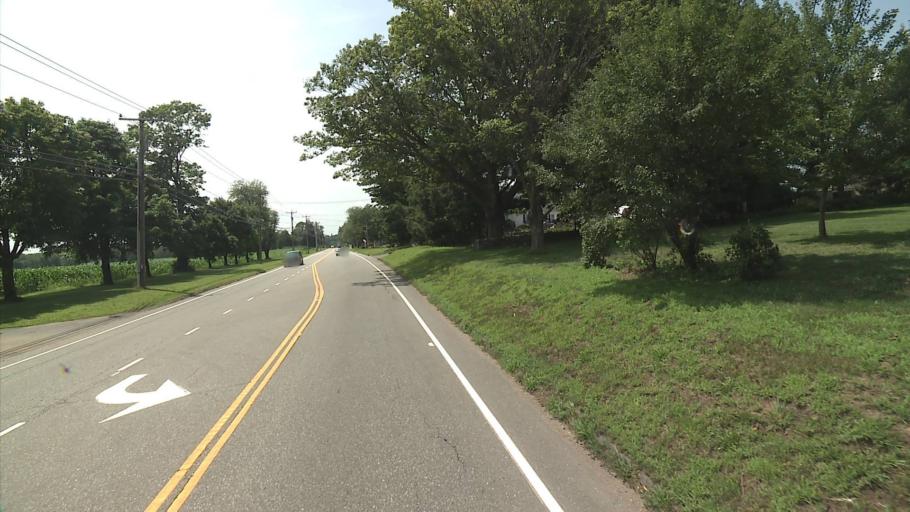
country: US
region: Connecticut
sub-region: Tolland County
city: Coventry Lake
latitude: 41.7985
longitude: -72.3870
